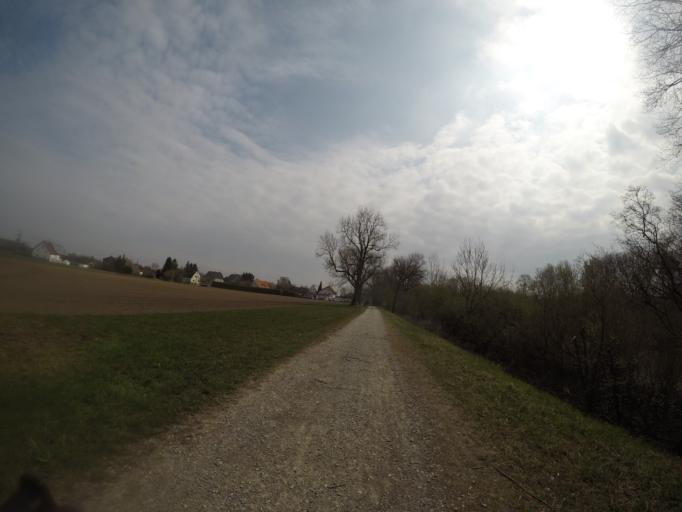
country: DE
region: Baden-Wuerttemberg
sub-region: Tuebingen Region
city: Ulm
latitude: 48.3710
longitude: 9.9853
